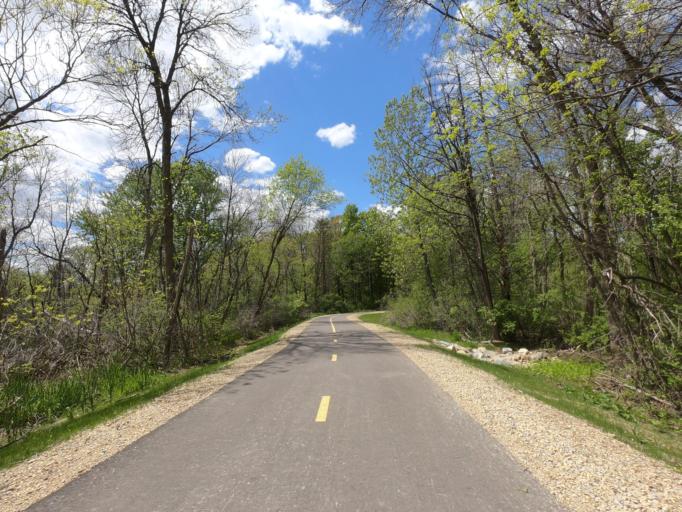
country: US
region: Wisconsin
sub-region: Dane County
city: Shorewood Hills
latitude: 43.0218
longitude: -89.4584
